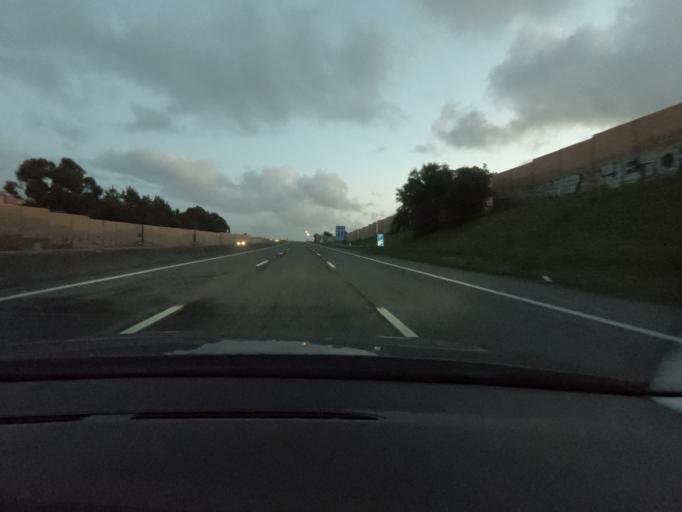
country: PT
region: Lisbon
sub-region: Sintra
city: Queluz
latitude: 38.7521
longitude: -9.2725
